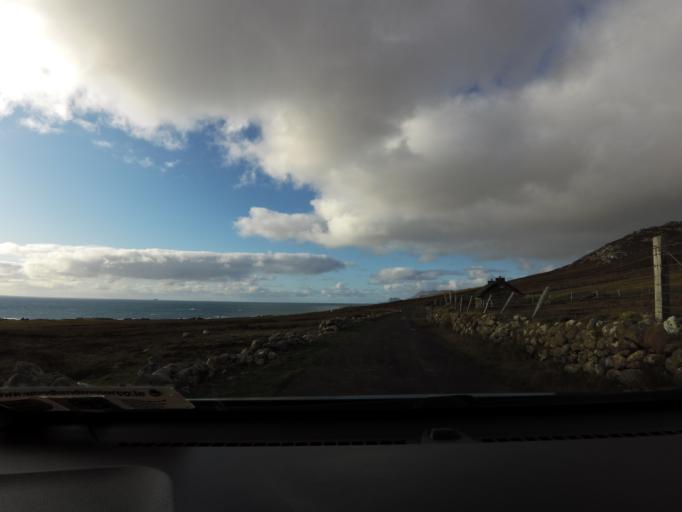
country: IE
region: Connaught
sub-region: Maigh Eo
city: Belmullet
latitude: 53.8918
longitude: -9.9844
